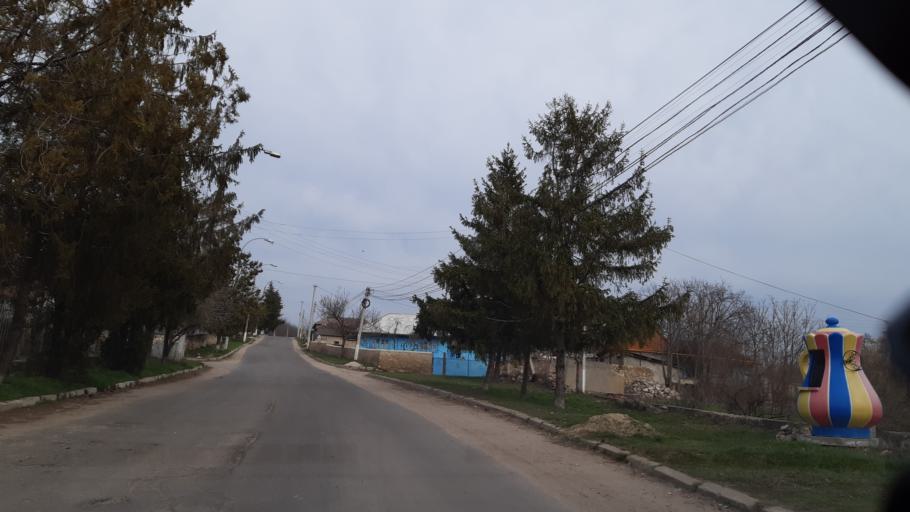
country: MD
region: Soldanesti
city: Soldanesti
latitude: 47.6841
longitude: 28.7649
